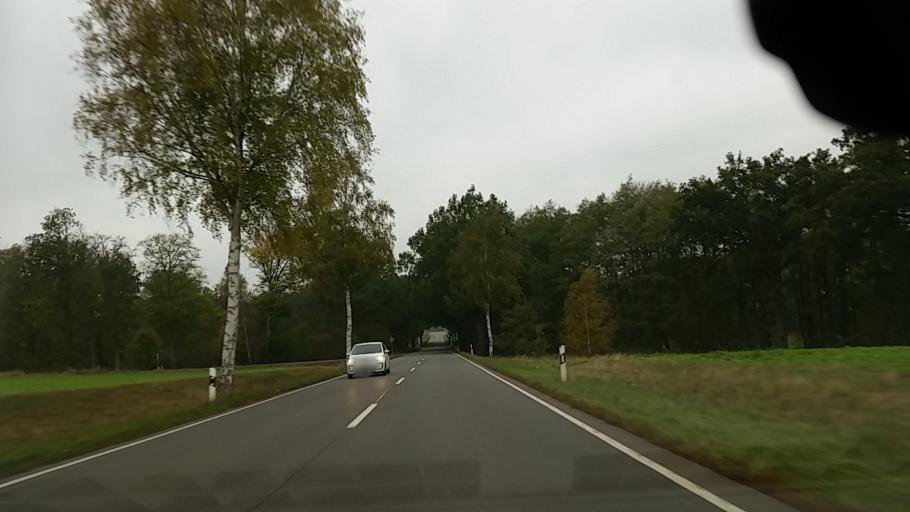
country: DE
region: Lower Saxony
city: Wieren
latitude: 52.9159
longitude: 10.6230
